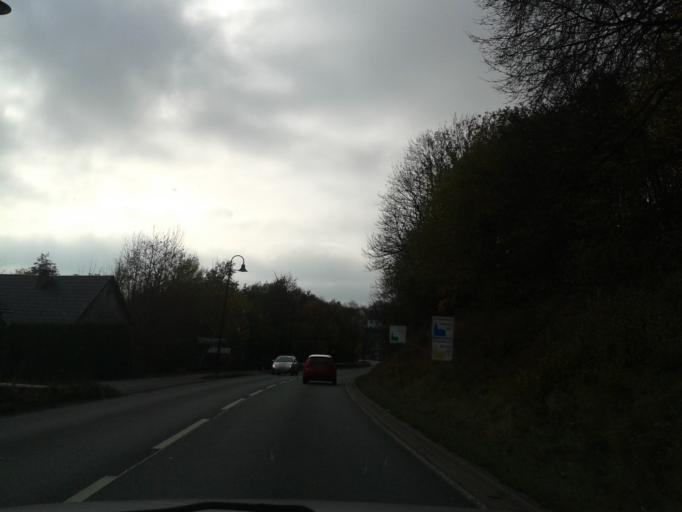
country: DE
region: North Rhine-Westphalia
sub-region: Regierungsbezirk Arnsberg
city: Bad Berleburg
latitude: 51.0604
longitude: 8.3956
